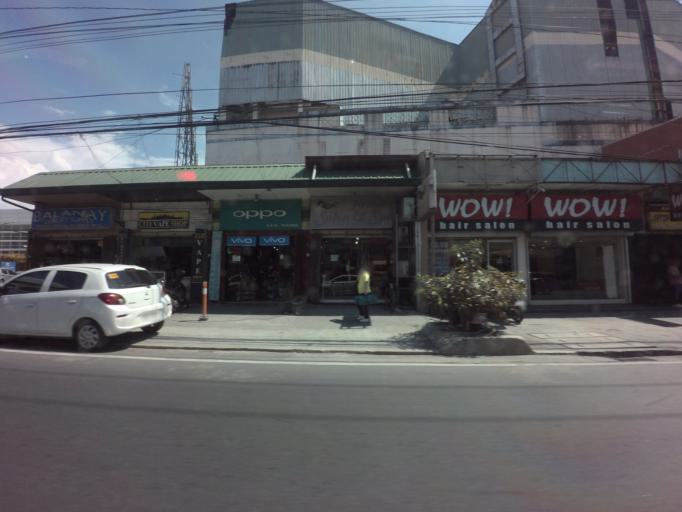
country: PH
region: Calabarzon
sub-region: Province of Rizal
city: Las Pinas
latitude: 14.4502
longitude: 120.9801
